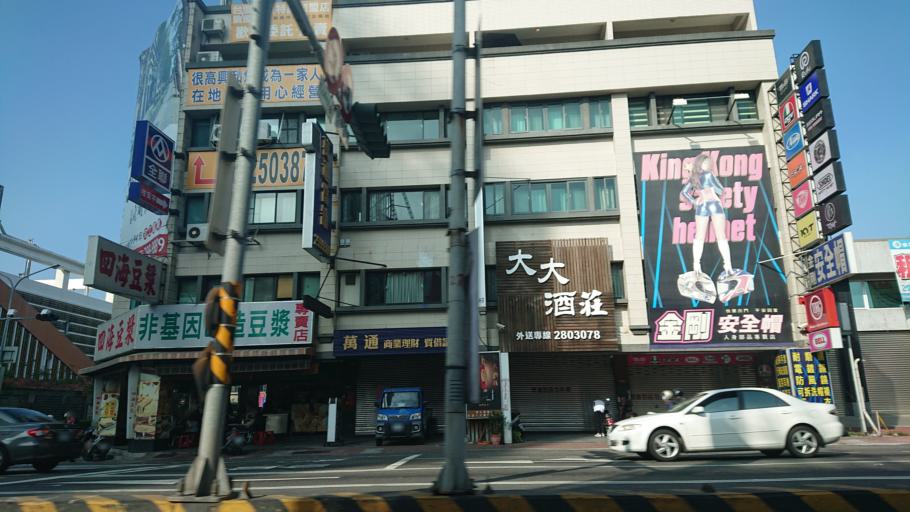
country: TW
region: Taiwan
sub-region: Tainan
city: Tainan
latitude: 22.9991
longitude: 120.1868
